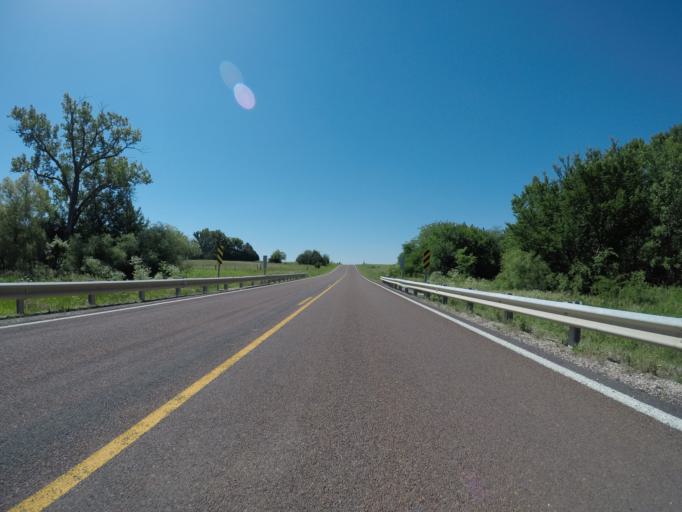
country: US
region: Kansas
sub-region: Morris County
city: Council Grove
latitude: 38.8096
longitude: -96.5943
